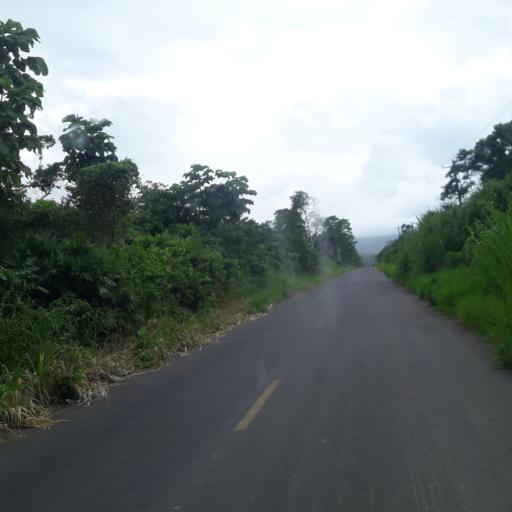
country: EC
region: Napo
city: Tena
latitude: -1.0485
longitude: -77.6637
